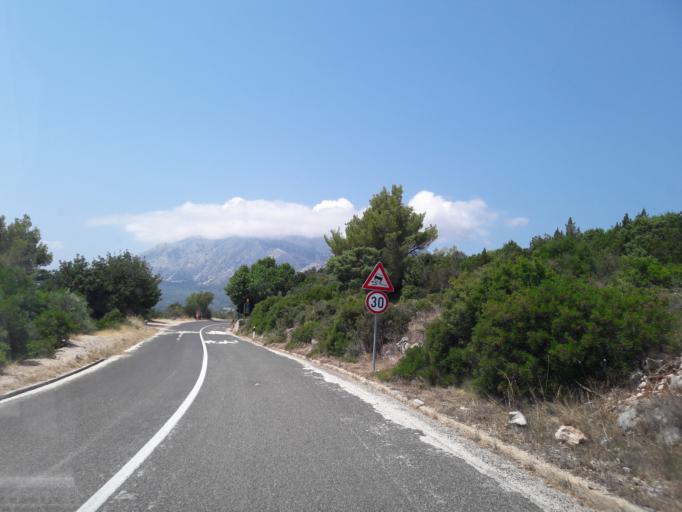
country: HR
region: Dubrovacko-Neretvanska
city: Orebic
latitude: 42.9768
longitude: 17.2298
